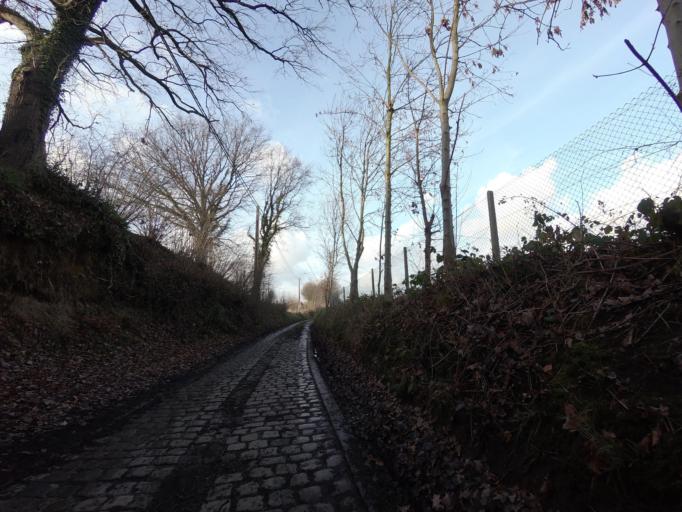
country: BE
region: Flanders
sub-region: Provincie Vlaams-Brabant
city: Bertem
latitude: 50.8832
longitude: 4.6037
